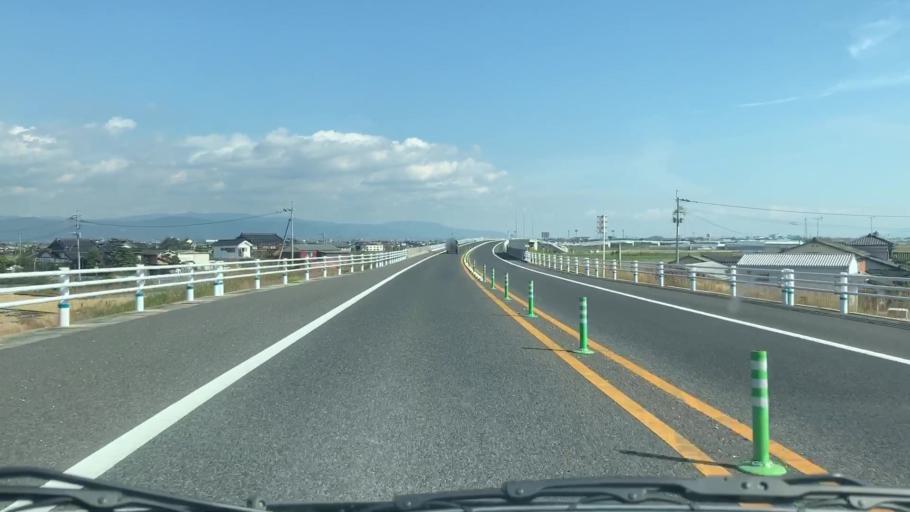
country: JP
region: Saga Prefecture
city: Saga-shi
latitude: 33.2273
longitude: 130.2195
